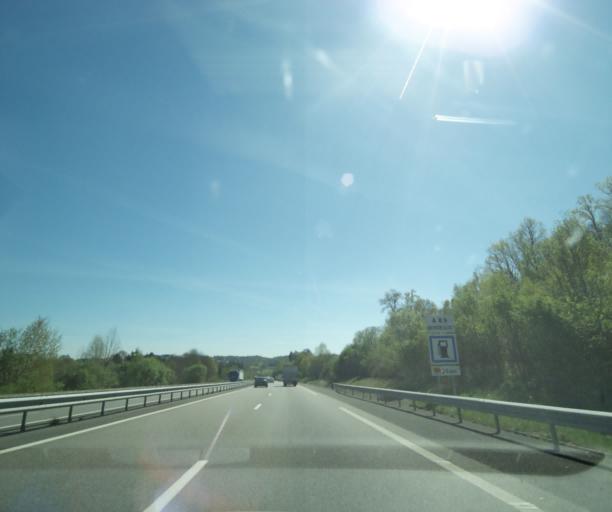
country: FR
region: Limousin
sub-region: Departement de la Correze
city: Vigeois
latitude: 45.3494
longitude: 1.5697
